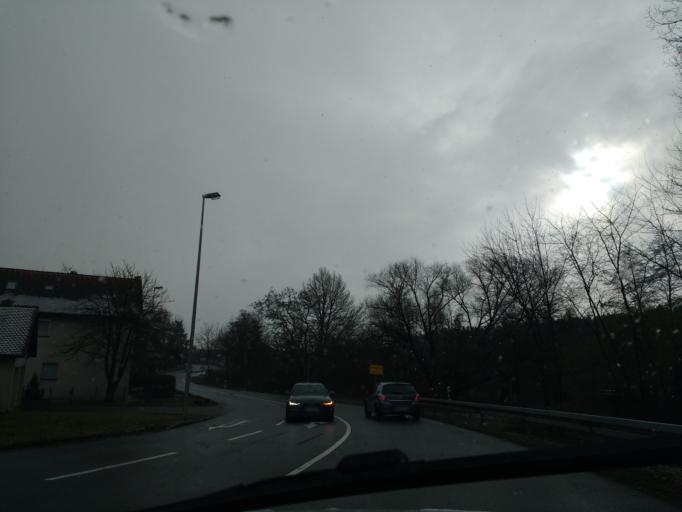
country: DE
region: Bavaria
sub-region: Regierungsbezirk Mittelfranken
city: Herzogenaurach
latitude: 49.5746
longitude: 10.8630
